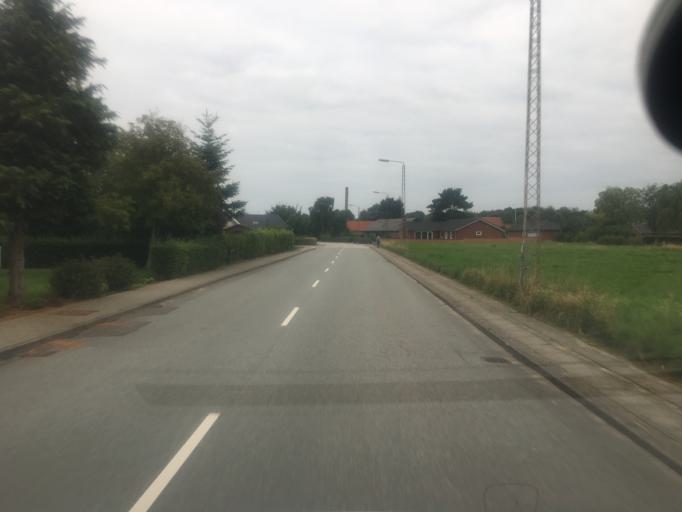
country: DK
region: South Denmark
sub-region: Tonder Kommune
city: Logumkloster
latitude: 55.0571
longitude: 8.9608
